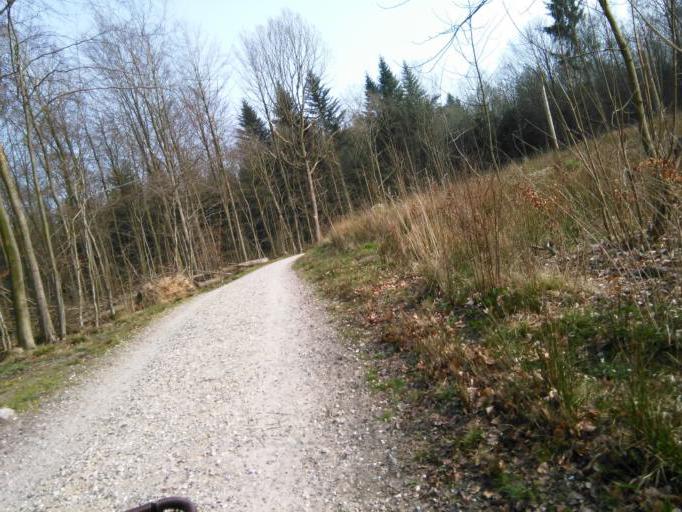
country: DK
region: Central Jutland
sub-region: Arhus Kommune
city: Beder
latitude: 56.0799
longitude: 10.2461
